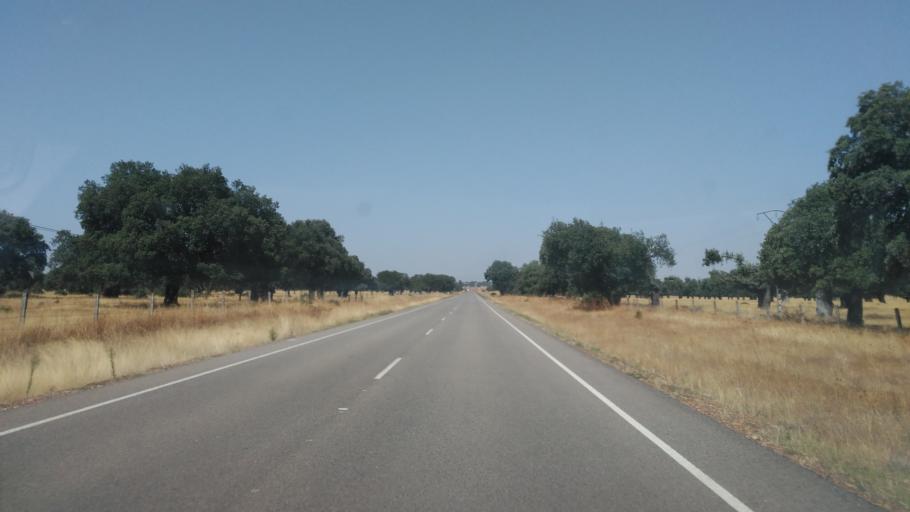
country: ES
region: Castille and Leon
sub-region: Provincia de Salamanca
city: Cabrillas
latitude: 40.7298
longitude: -6.1623
